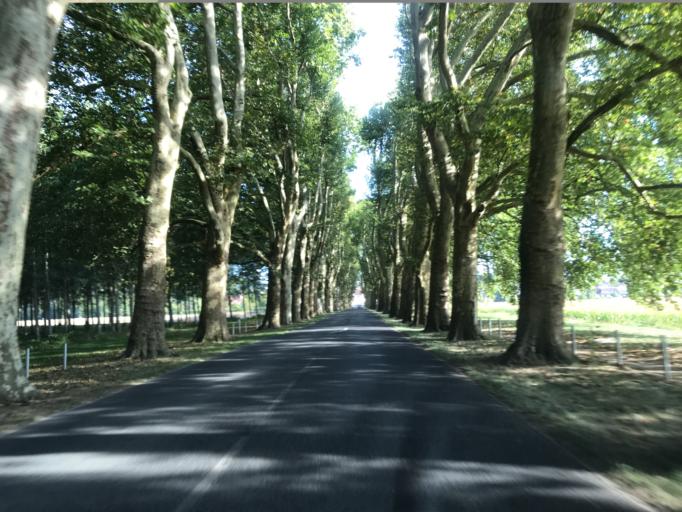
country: FR
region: Champagne-Ardenne
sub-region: Departement de la Marne
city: Damery
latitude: 49.0651
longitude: 3.8753
